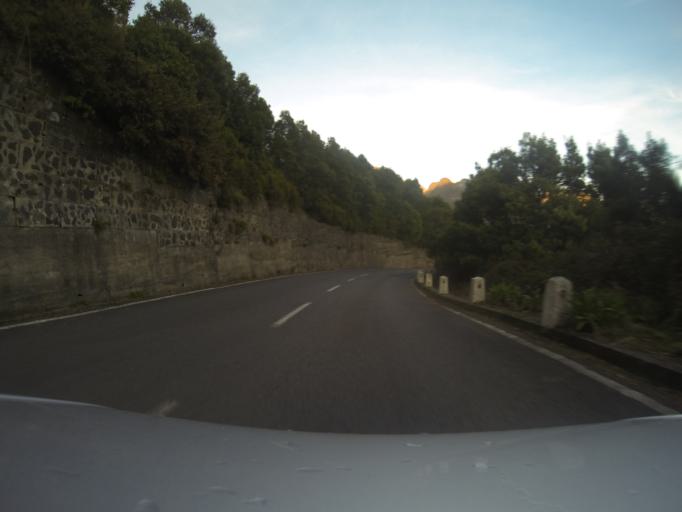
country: PT
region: Madeira
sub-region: Sao Vicente
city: Sao Vicente
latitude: 32.7546
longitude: -17.0212
